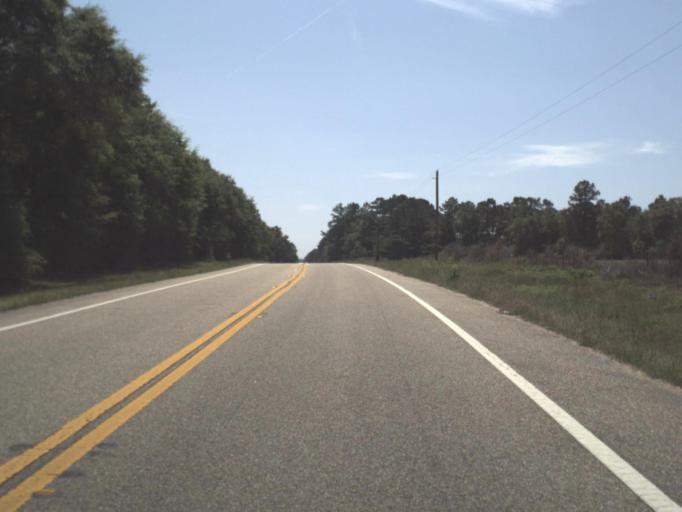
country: US
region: Florida
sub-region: Jackson County
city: Marianna
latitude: 30.6548
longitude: -85.2151
